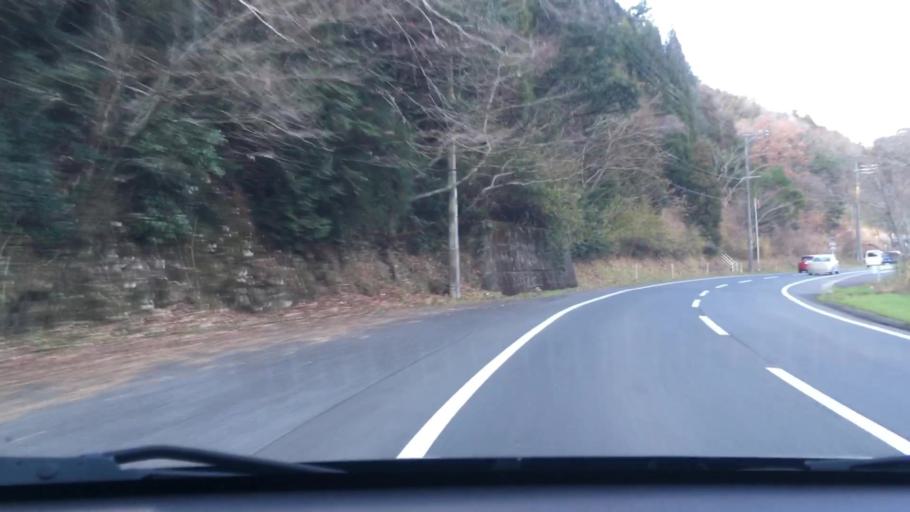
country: JP
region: Oita
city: Bungo-Takada-shi
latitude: 33.4704
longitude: 131.3850
